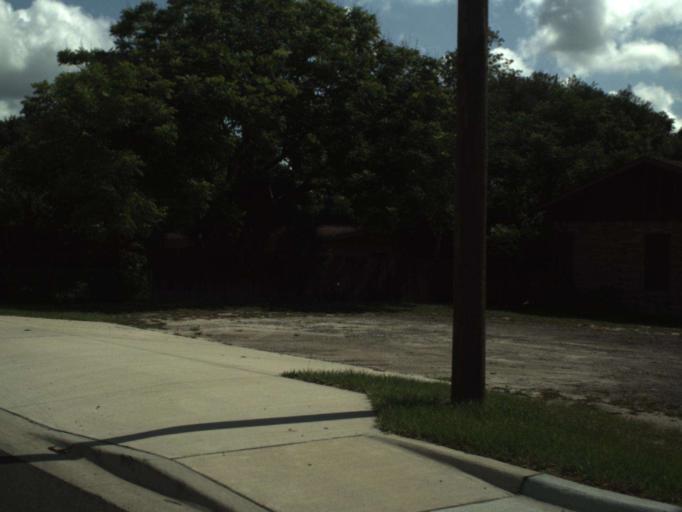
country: US
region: Florida
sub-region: Seminole County
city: Midway
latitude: 28.8503
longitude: -81.1620
